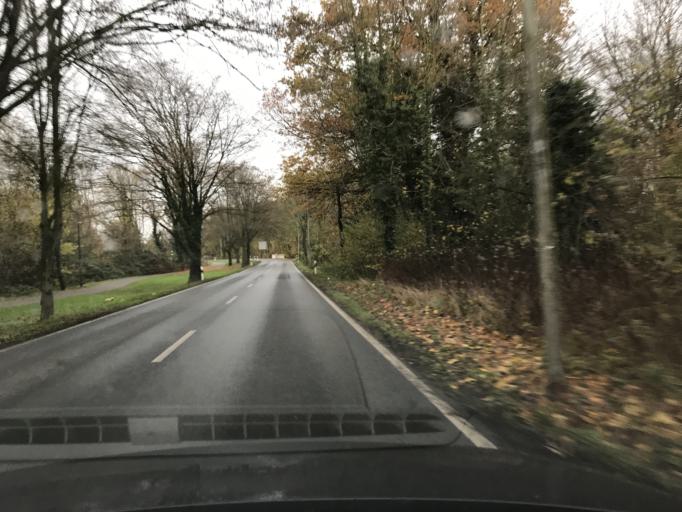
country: DE
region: North Rhine-Westphalia
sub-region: Regierungsbezirk Arnsberg
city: Hamm
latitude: 51.6970
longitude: 7.8382
